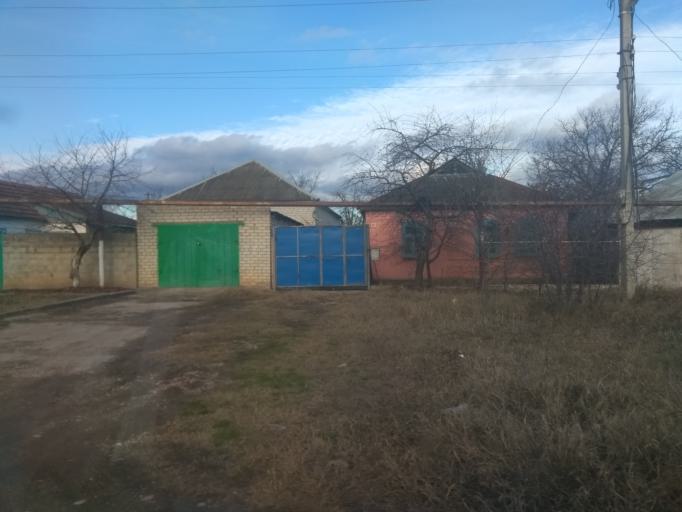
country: RU
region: Stavropol'skiy
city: Krasnokumskoye
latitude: 44.1758
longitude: 43.4844
